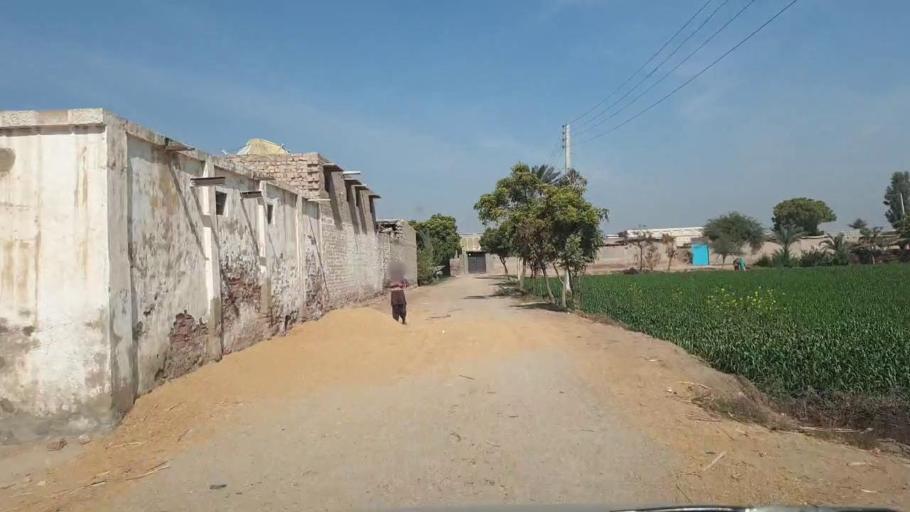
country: PK
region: Sindh
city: Chambar
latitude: 25.3860
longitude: 68.7929
